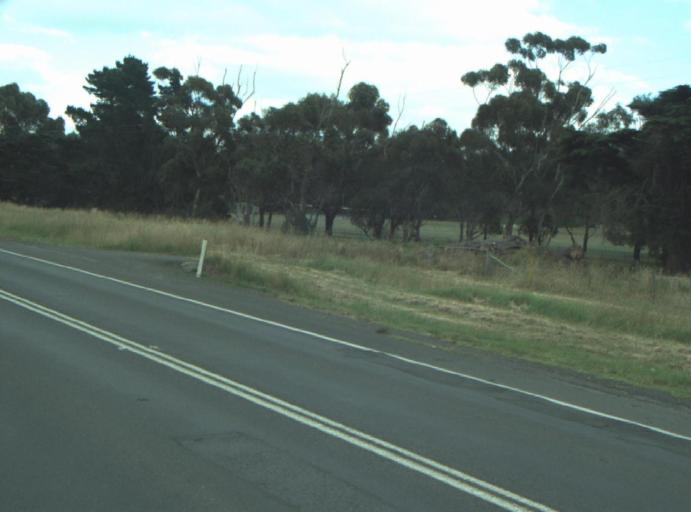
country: AU
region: Victoria
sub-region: Greater Geelong
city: Wandana Heights
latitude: -38.2045
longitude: 144.2980
